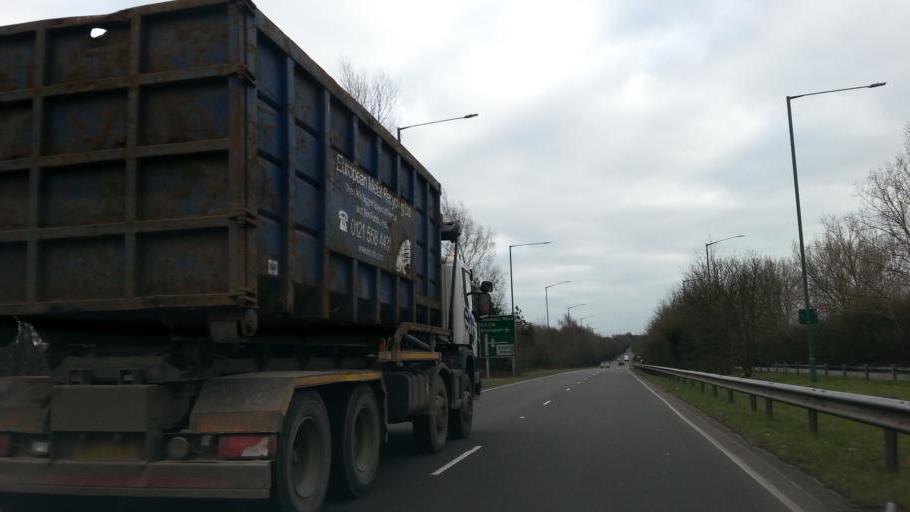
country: GB
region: England
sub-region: Warwickshire
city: Water Orton
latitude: 52.5049
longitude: -1.7429
